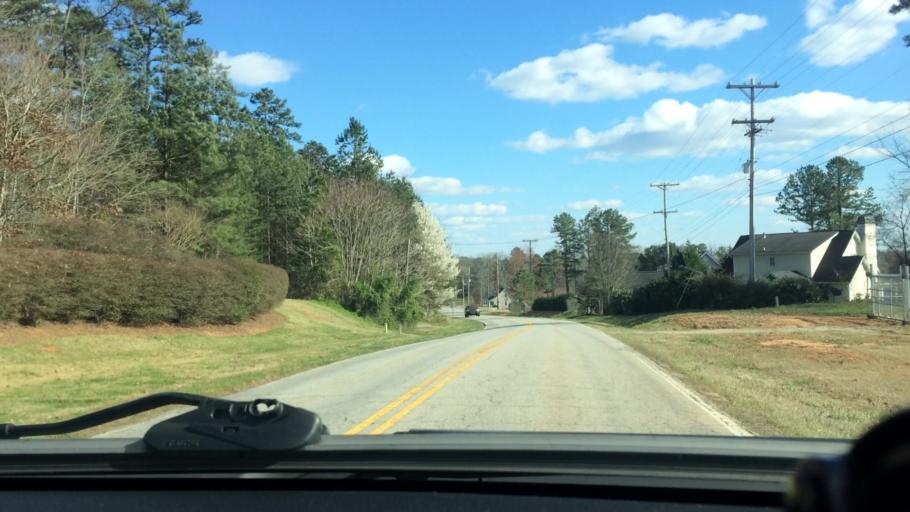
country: US
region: South Carolina
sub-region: Anderson County
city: Powdersville
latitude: 34.7976
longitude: -82.5433
